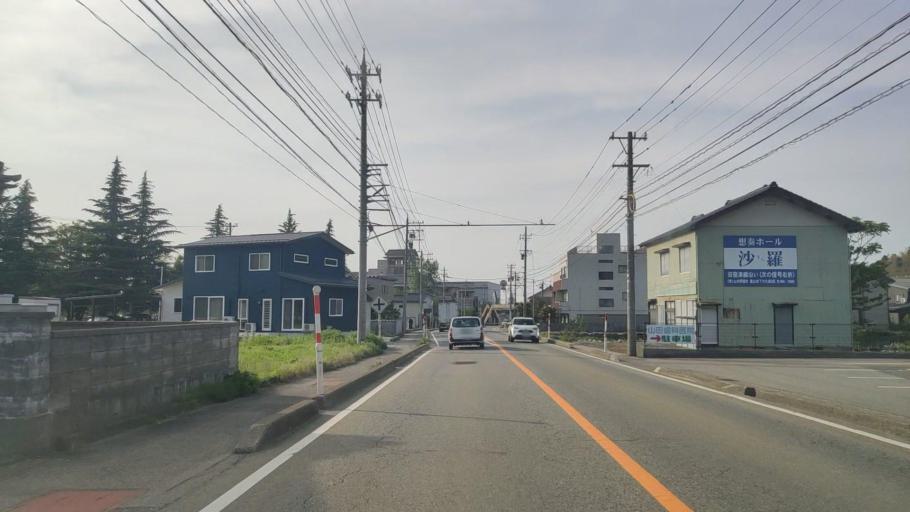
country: JP
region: Toyama
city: Yatsuomachi-higashikumisaka
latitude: 36.5755
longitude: 137.2082
